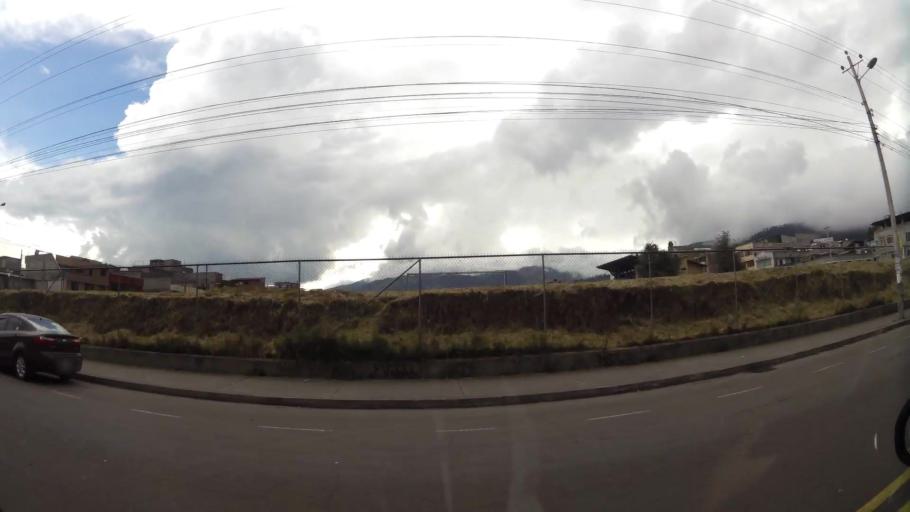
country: EC
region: Pichincha
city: Quito
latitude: -0.2598
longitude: -78.5396
